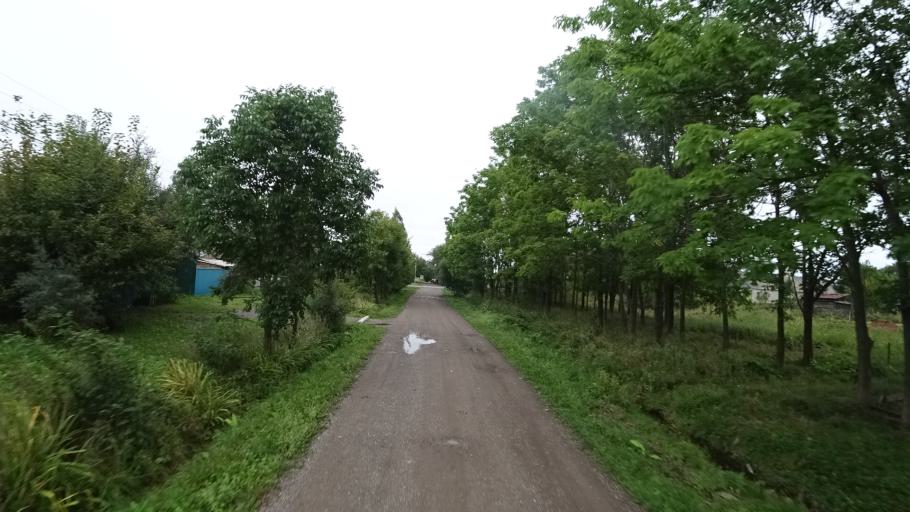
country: RU
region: Primorskiy
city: Chernigovka
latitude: 44.3385
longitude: 132.5433
